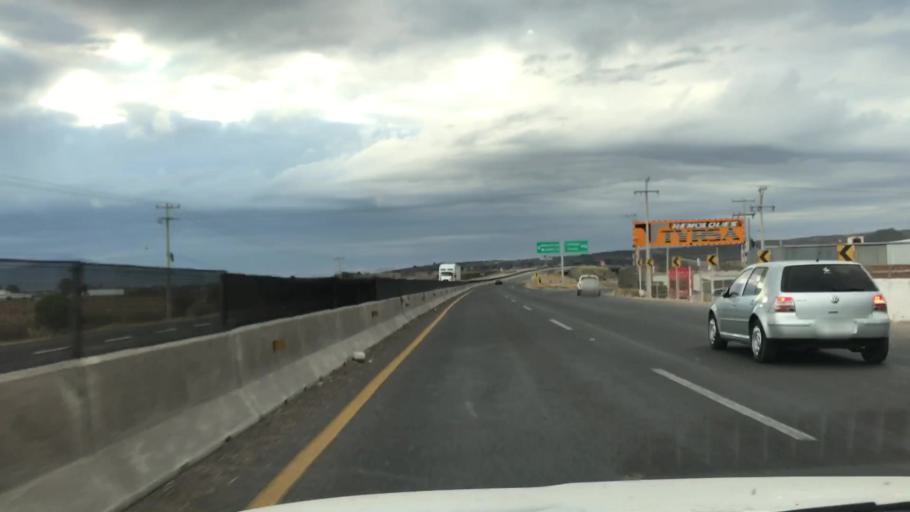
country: MX
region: Guanajuato
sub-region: Penjamo
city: Estacion la Piedad
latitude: 20.3881
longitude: -101.9469
